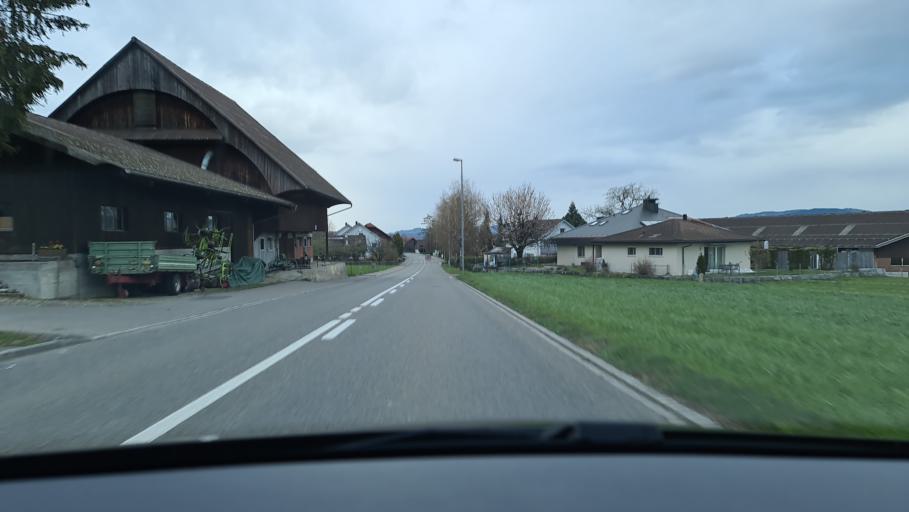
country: CH
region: Aargau
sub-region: Bezirk Muri
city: Auw
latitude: 47.2225
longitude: 8.3645
